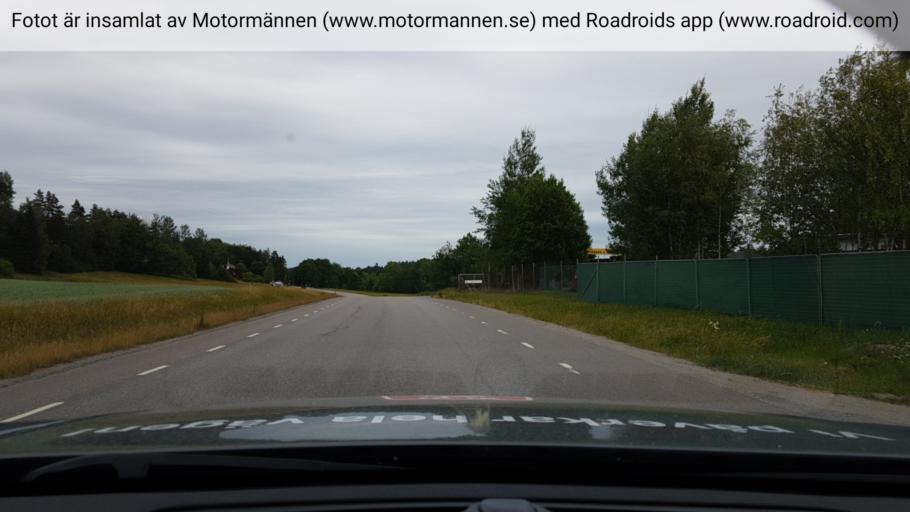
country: SE
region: Stockholm
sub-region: Nynashamns Kommun
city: Osmo
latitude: 59.0046
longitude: 17.9530
